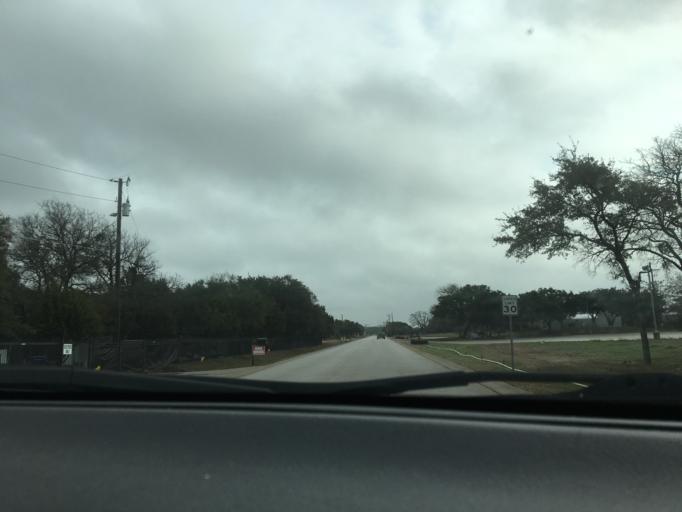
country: US
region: Texas
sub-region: Hays County
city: Dripping Springs
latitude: 30.1852
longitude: -98.0859
